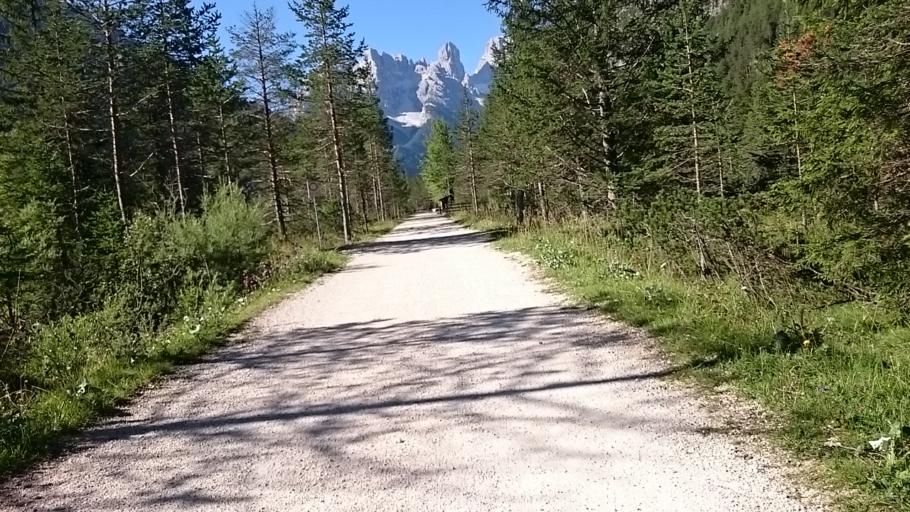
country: IT
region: Trentino-Alto Adige
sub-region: Bolzano
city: Dobbiaco
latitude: 46.6396
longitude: 12.2327
